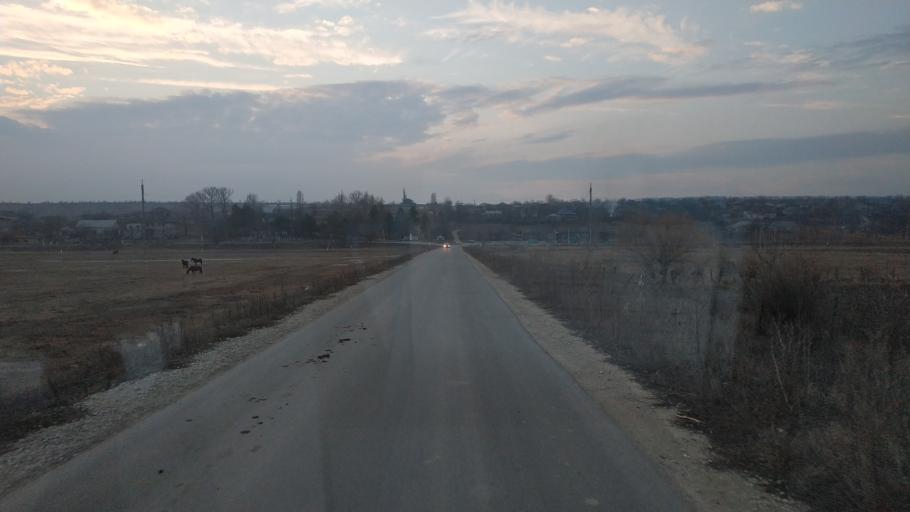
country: MD
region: Hincesti
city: Dancu
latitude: 46.6604
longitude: 28.3104
